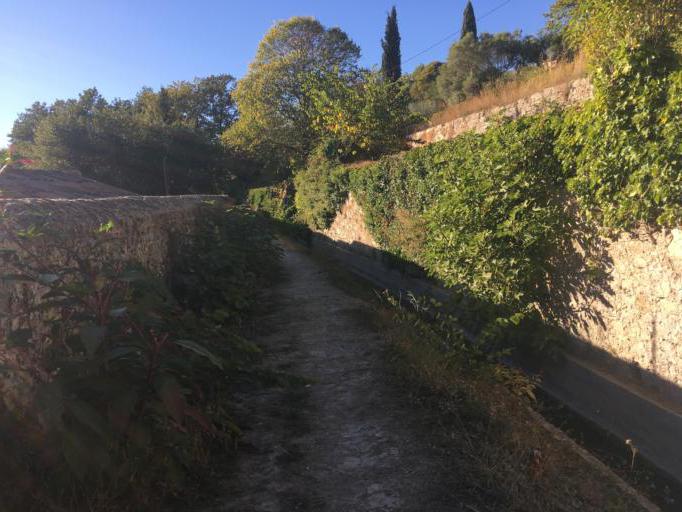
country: FR
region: Provence-Alpes-Cote d'Azur
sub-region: Departement du Var
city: Draguignan
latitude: 43.5441
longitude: 6.4601
